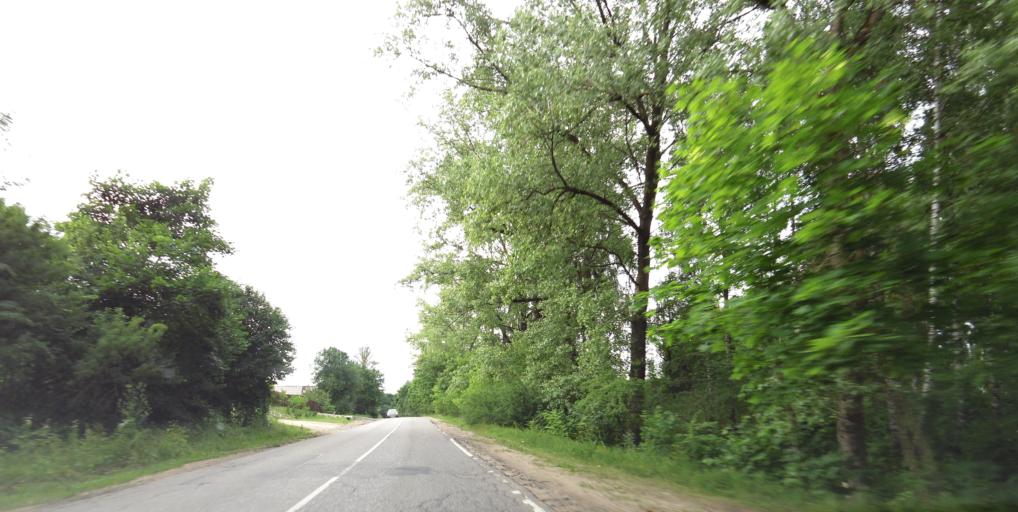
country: LT
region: Vilnius County
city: Justiniskes
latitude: 54.7133
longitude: 25.1989
